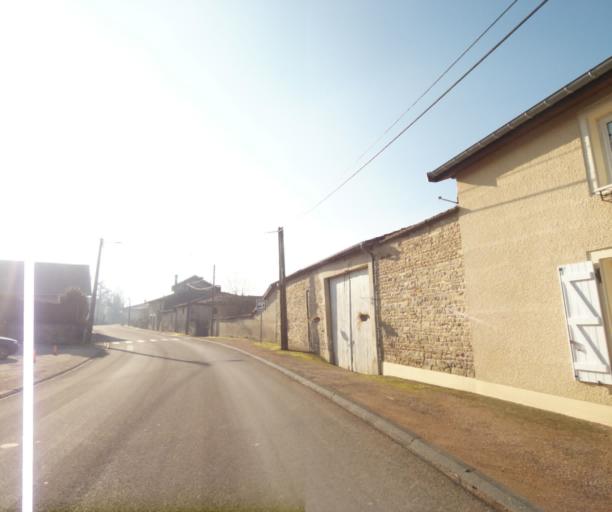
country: FR
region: Champagne-Ardenne
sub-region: Departement de la Haute-Marne
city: Wassy
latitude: 48.4574
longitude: 4.9641
